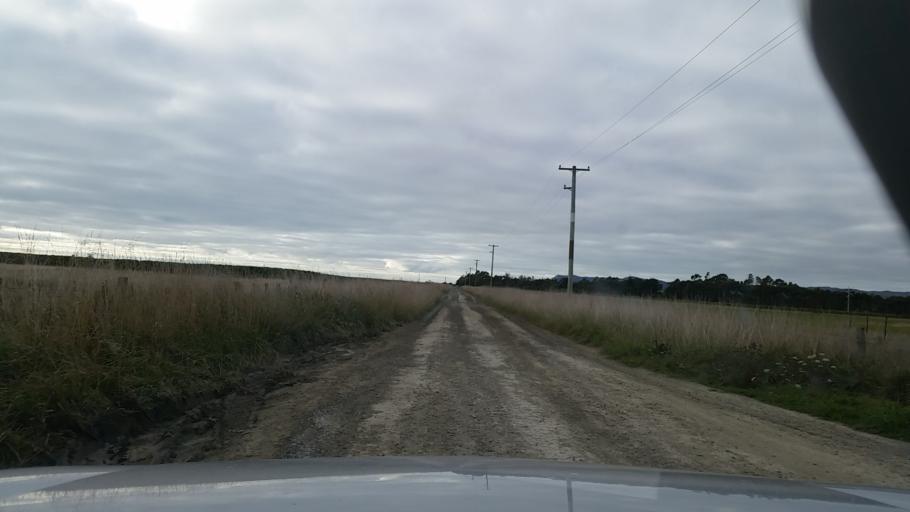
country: NZ
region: Marlborough
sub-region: Marlborough District
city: Blenheim
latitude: -41.5102
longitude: 174.0343
